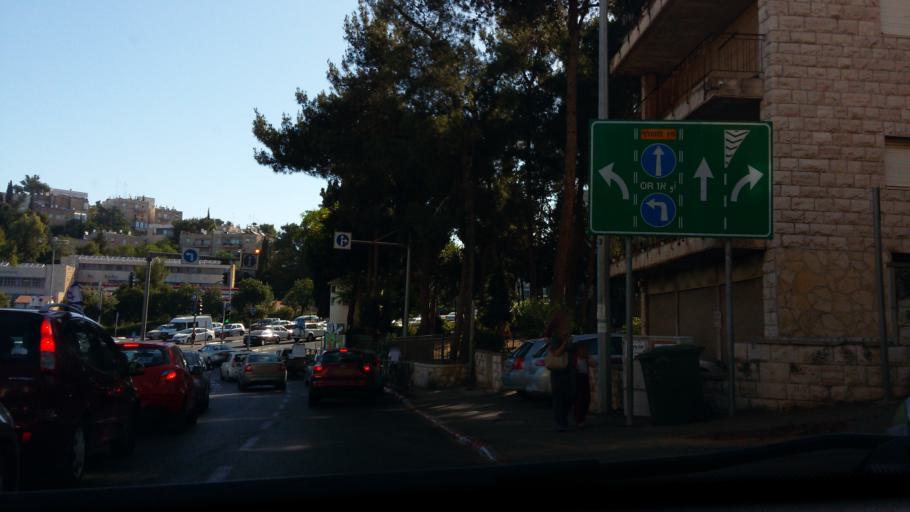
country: IL
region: Jerusalem
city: Jerusalem
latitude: 31.7690
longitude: 35.2087
